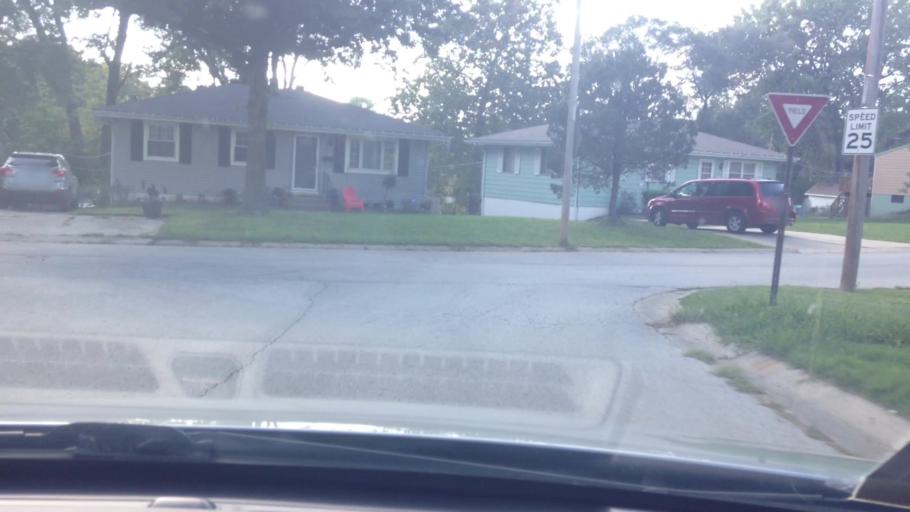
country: US
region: Missouri
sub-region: Clay County
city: Claycomo
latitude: 39.1774
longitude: -94.4968
